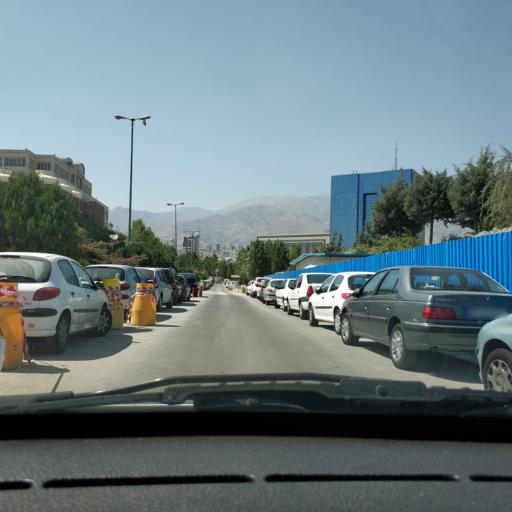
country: IR
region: Tehran
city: Tajrish
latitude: 35.7541
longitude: 51.4353
